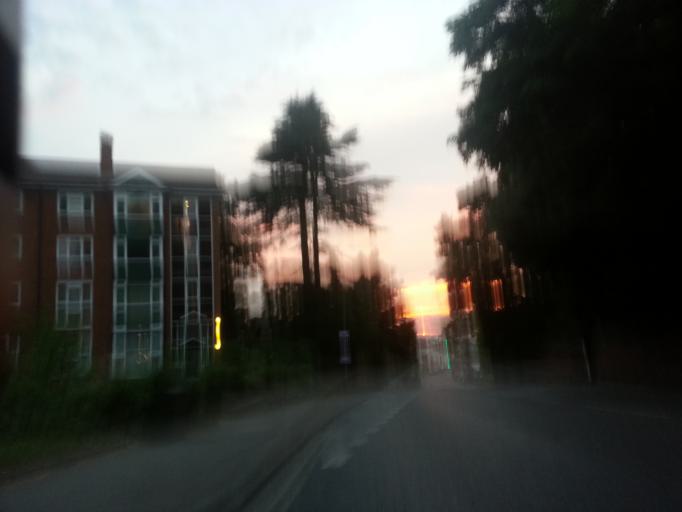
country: GB
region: England
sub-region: Suffolk
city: Ipswich
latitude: 52.0498
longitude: 1.1713
